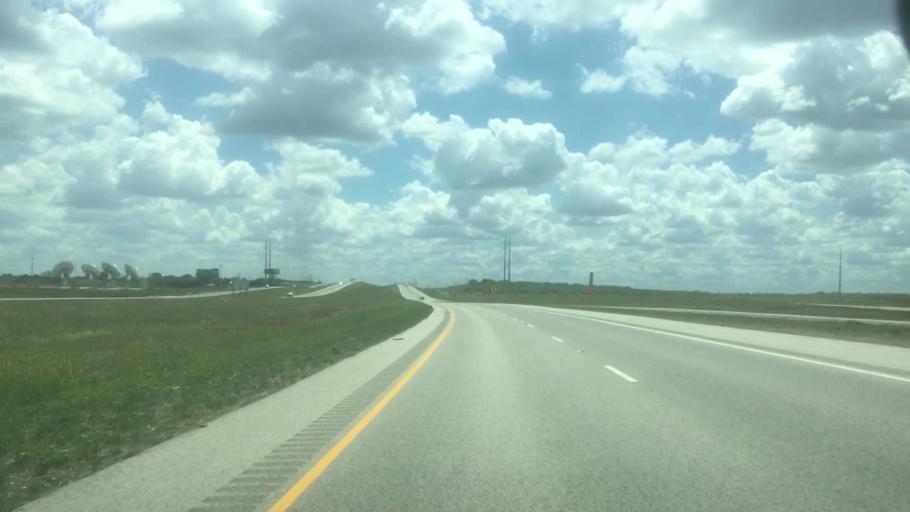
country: US
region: Texas
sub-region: Caldwell County
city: Uhland
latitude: 30.0147
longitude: -97.6884
